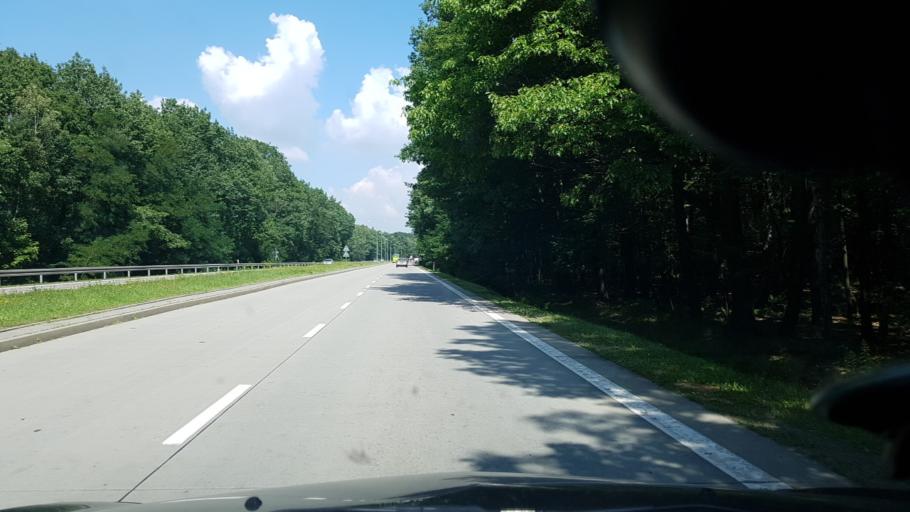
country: PL
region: Silesian Voivodeship
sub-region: Zory
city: Zory
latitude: 50.0570
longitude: 18.7220
